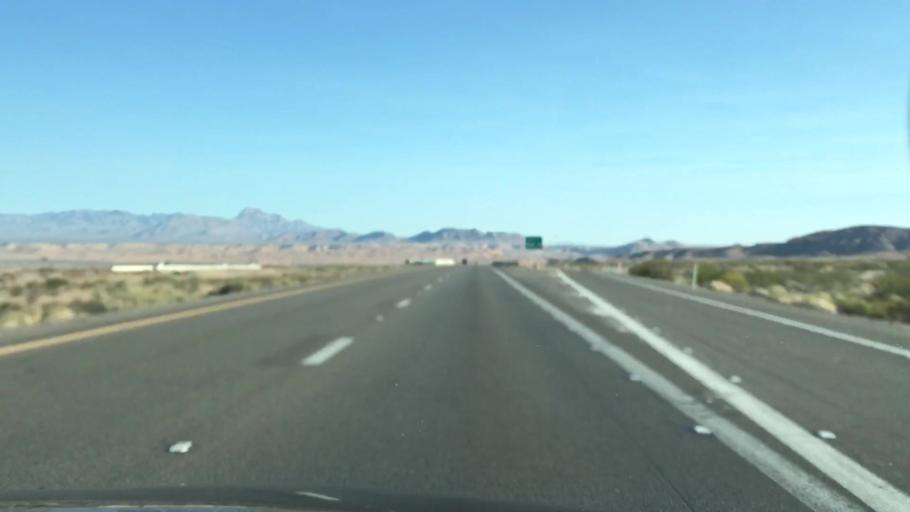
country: US
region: Nevada
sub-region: Clark County
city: Moapa Town
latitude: 36.6350
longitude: -114.6011
